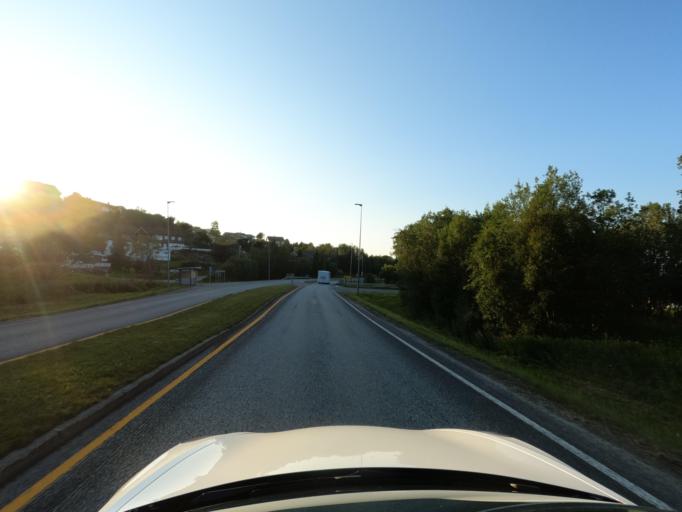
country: NO
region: Troms
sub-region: Harstad
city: Harstad
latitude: 68.7537
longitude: 16.5667
